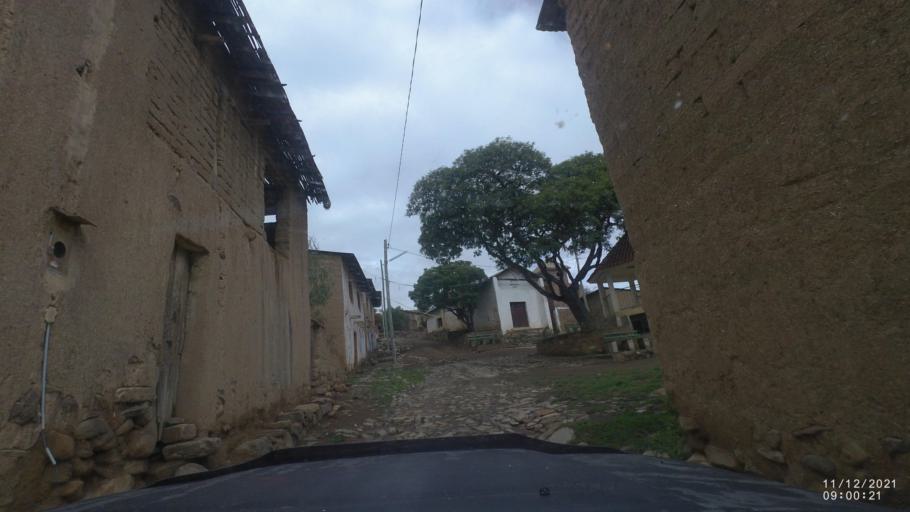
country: BO
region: Cochabamba
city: Tarata
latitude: -17.9008
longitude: -65.9440
